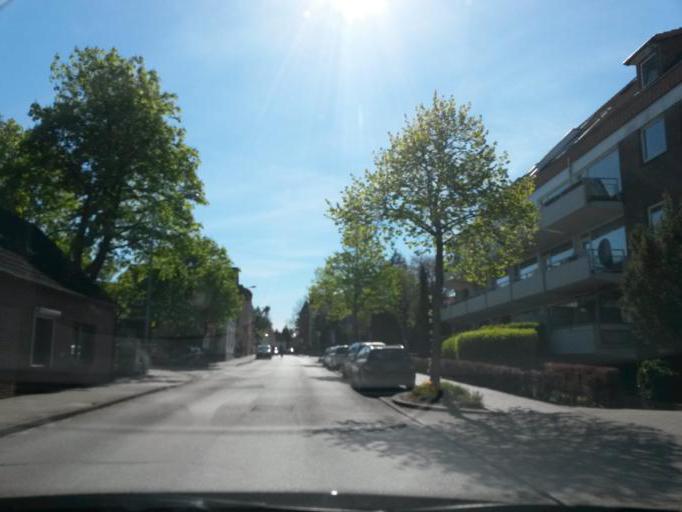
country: DE
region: Schleswig-Holstein
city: Wedel
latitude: 53.5851
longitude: 9.7017
